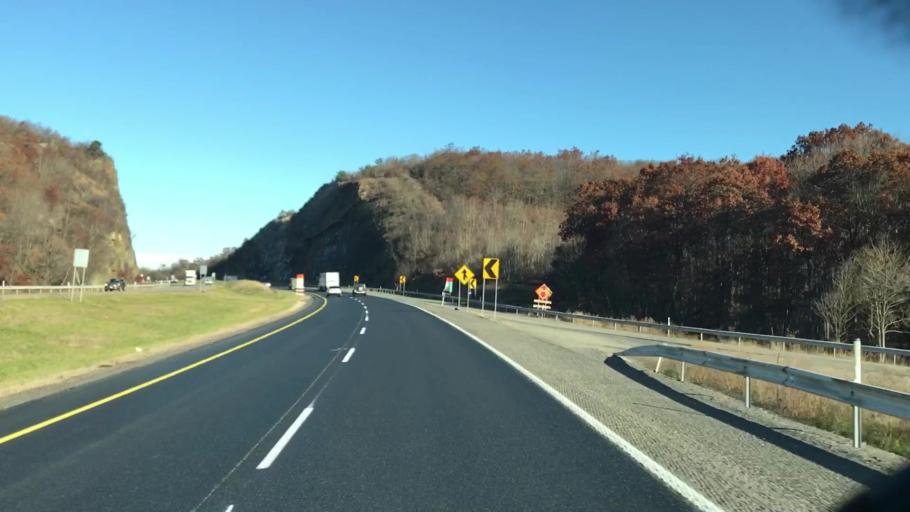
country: US
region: Pennsylvania
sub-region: Schuylkill County
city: McAdoo
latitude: 40.8850
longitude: -76.0177
